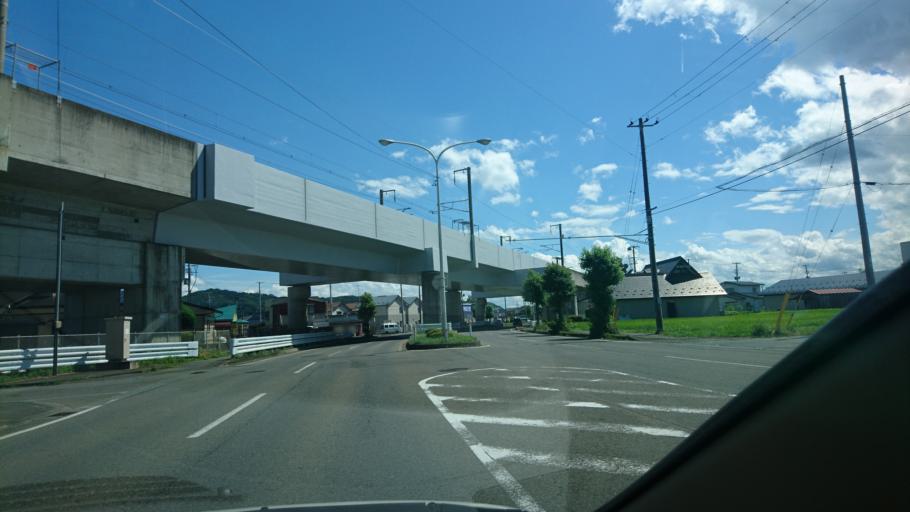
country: JP
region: Iwate
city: Kitakami
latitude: 39.2939
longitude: 141.1296
